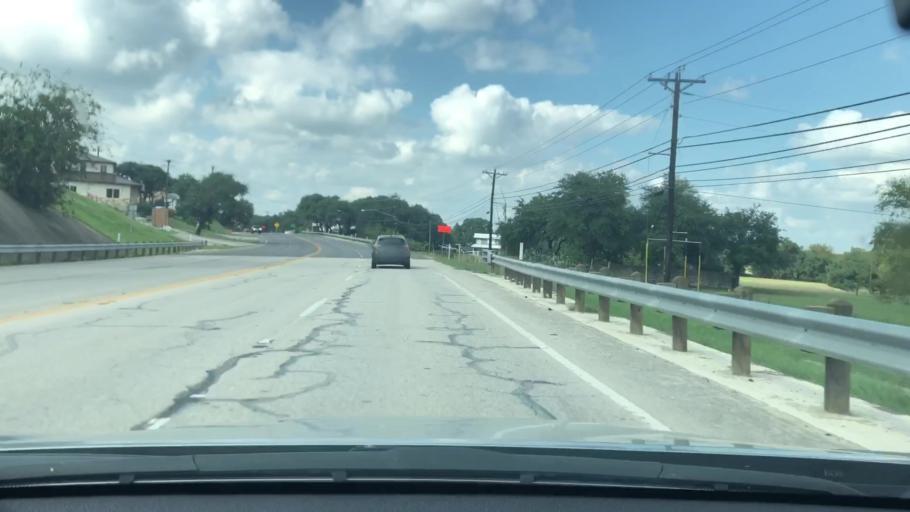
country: US
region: Texas
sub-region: Kendall County
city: Boerne
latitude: 29.7719
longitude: -98.7204
